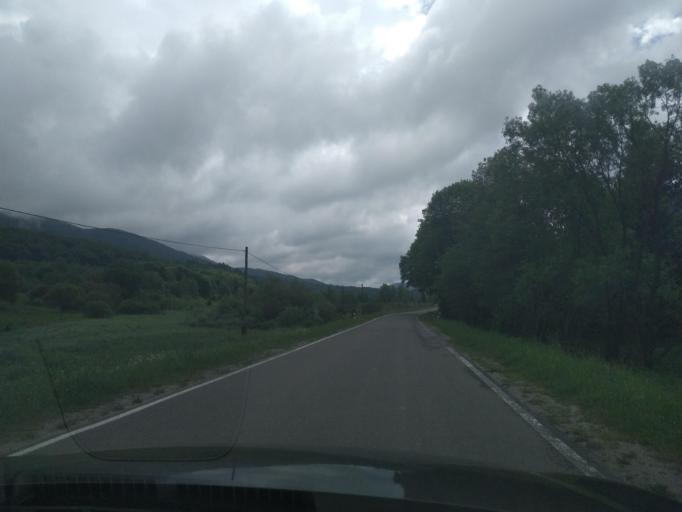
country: PL
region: Subcarpathian Voivodeship
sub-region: Powiat bieszczadzki
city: Lutowiska
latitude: 49.0810
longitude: 22.6555
